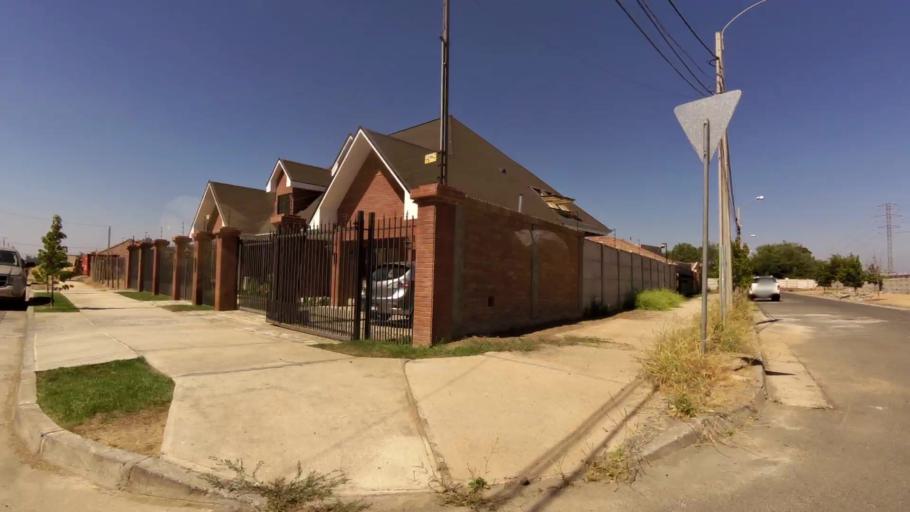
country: CL
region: Maule
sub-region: Provincia de Talca
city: Talca
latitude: -35.4404
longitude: -71.5969
